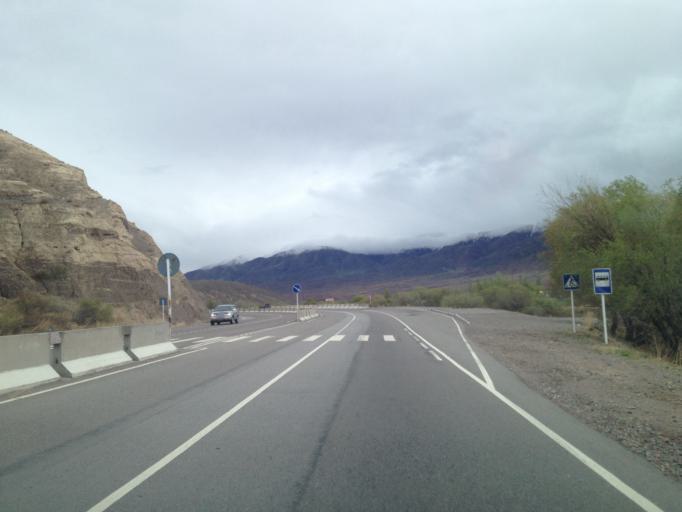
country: KG
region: Naryn
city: Kochkor
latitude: 42.4891
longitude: 75.8565
